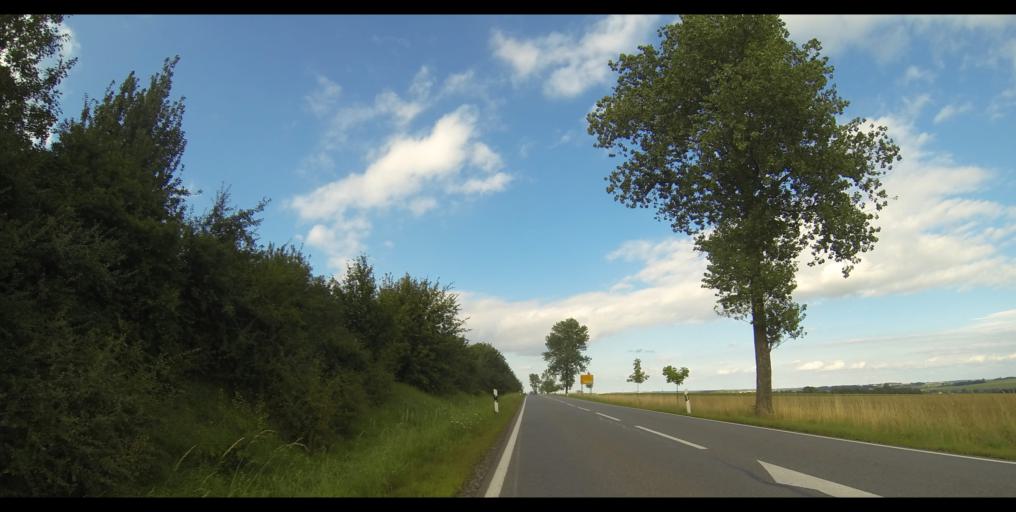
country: DE
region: Saxony
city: Hainichen
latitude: 50.9568
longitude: 13.0821
